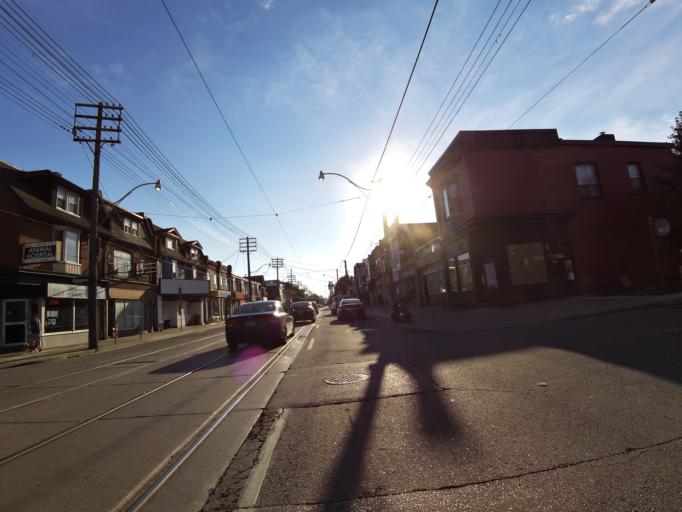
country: CA
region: Ontario
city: Toronto
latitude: 43.6690
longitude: -79.3366
